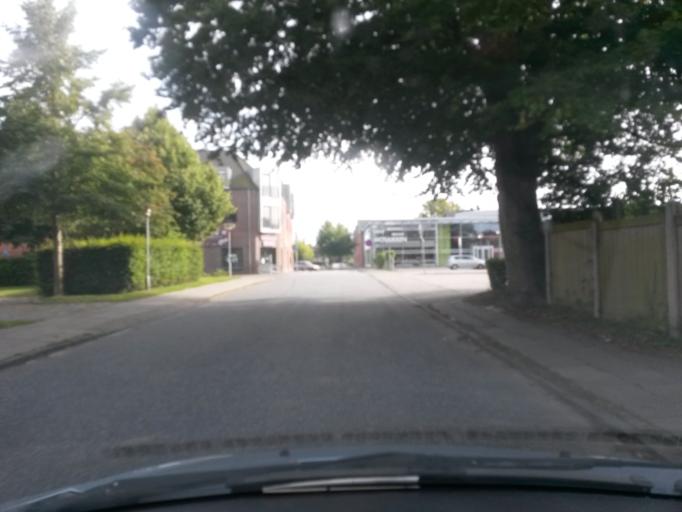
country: DK
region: Central Jutland
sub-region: Silkeborg Kommune
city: Kjellerup
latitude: 56.2882
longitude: 9.4286
